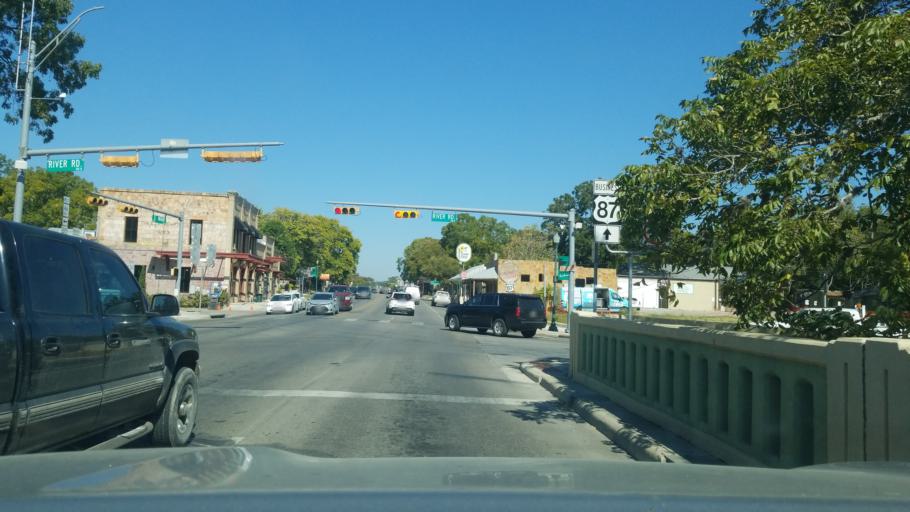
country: US
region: Texas
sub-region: Kendall County
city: Boerne
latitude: 29.7893
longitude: -98.7294
